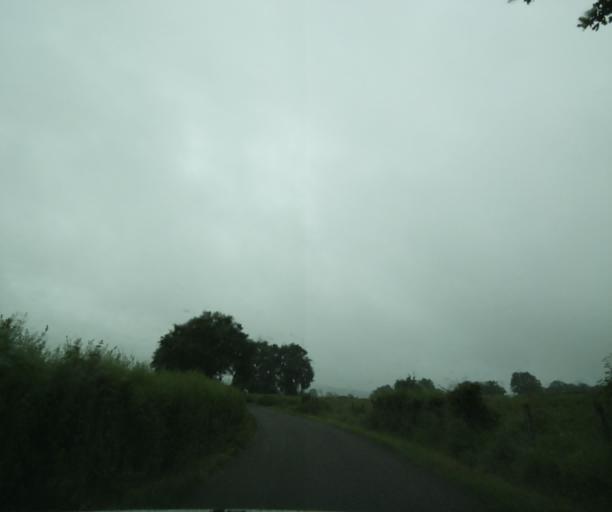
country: FR
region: Bourgogne
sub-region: Departement de Saone-et-Loire
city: Charolles
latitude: 46.4179
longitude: 4.2770
